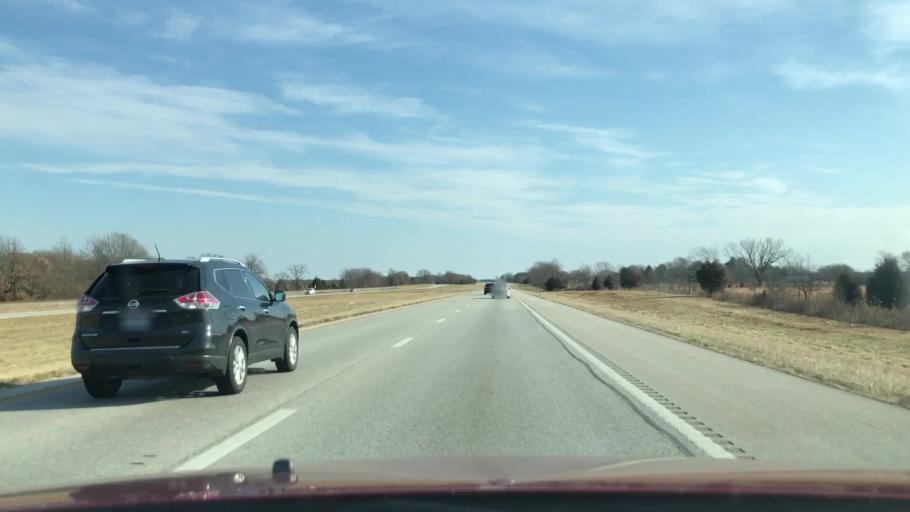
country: US
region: Missouri
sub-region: Webster County
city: Rogersville
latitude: 37.1223
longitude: -92.9979
